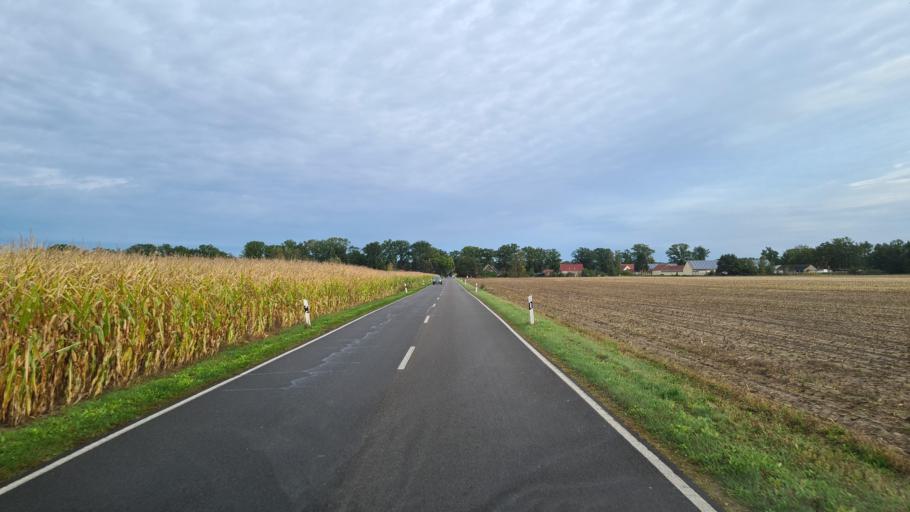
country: DE
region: Brandenburg
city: Kasel-Golzig
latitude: 51.9295
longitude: 13.7074
